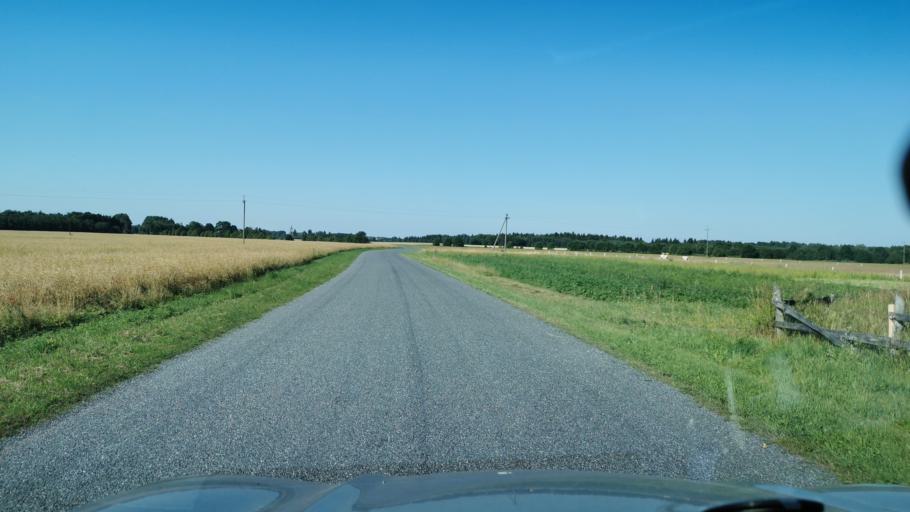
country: EE
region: Harju
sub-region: Paldiski linn
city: Paldiski
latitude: 59.2164
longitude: 24.0449
